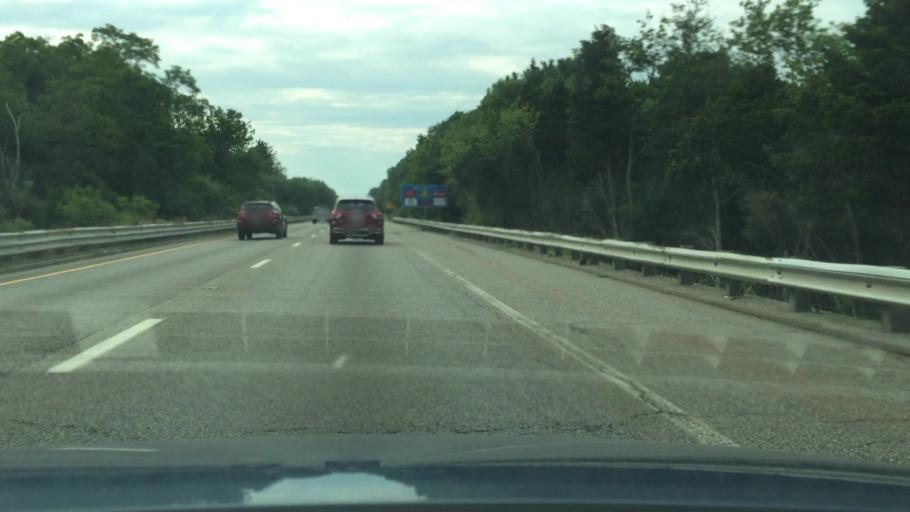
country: US
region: Massachusetts
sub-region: Plymouth County
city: Hanover
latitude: 42.1287
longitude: -70.8034
